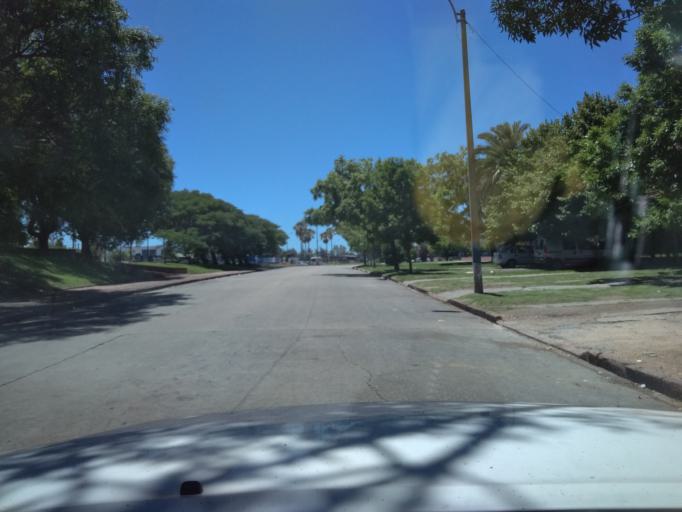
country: UY
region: Canelones
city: Paso de Carrasco
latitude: -34.8868
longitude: -56.1015
